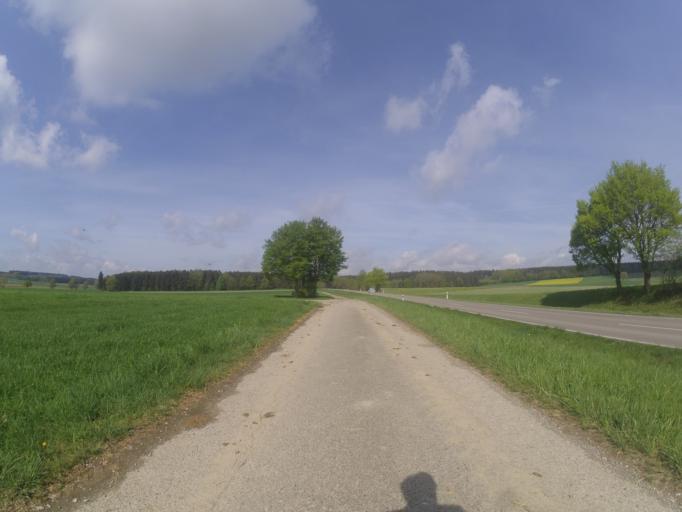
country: DE
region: Baden-Wuerttemberg
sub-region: Tuebingen Region
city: Griesingen
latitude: 48.2411
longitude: 9.8119
